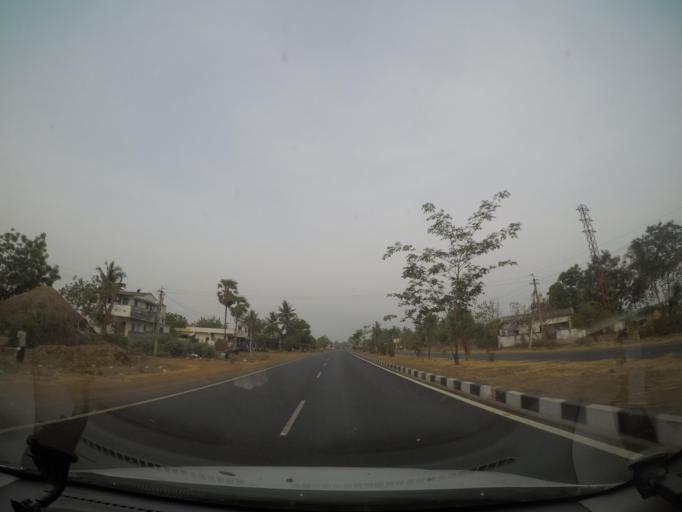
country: IN
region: Andhra Pradesh
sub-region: Krishna
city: Gannavaram
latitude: 16.6087
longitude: 80.9077
